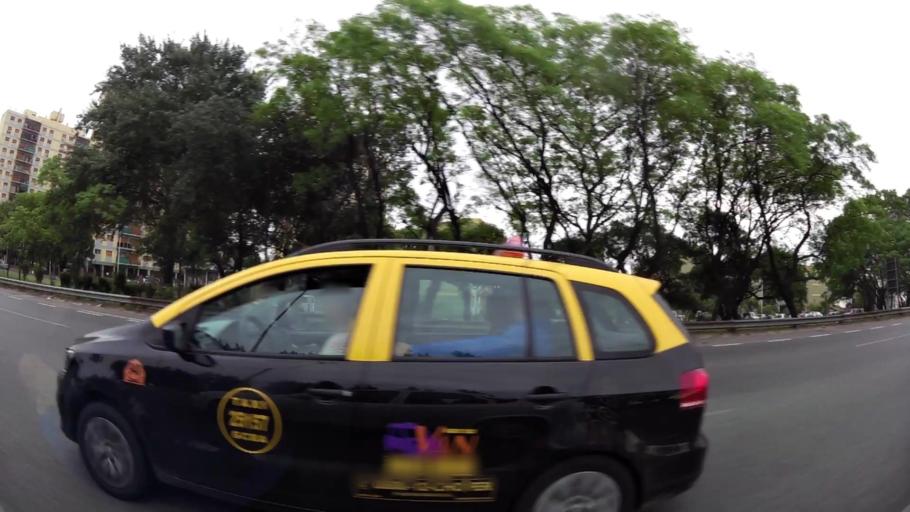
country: AR
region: Buenos Aires F.D.
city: Villa Lugano
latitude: -34.7048
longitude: -58.5004
